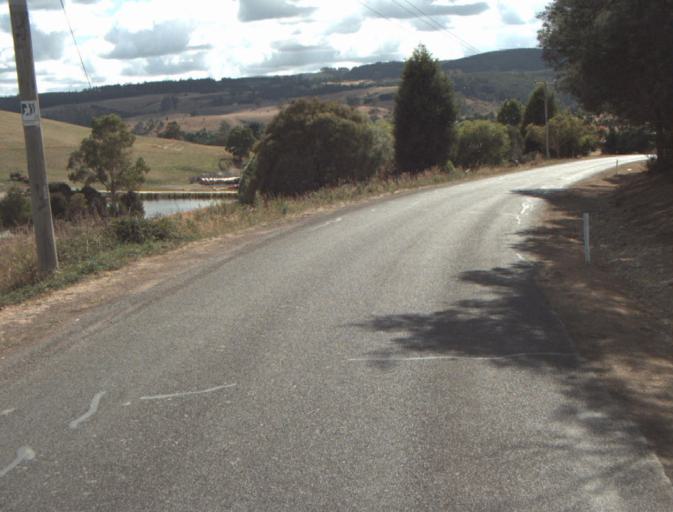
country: AU
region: Tasmania
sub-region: Launceston
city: Mayfield
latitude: -41.2569
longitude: 147.2092
